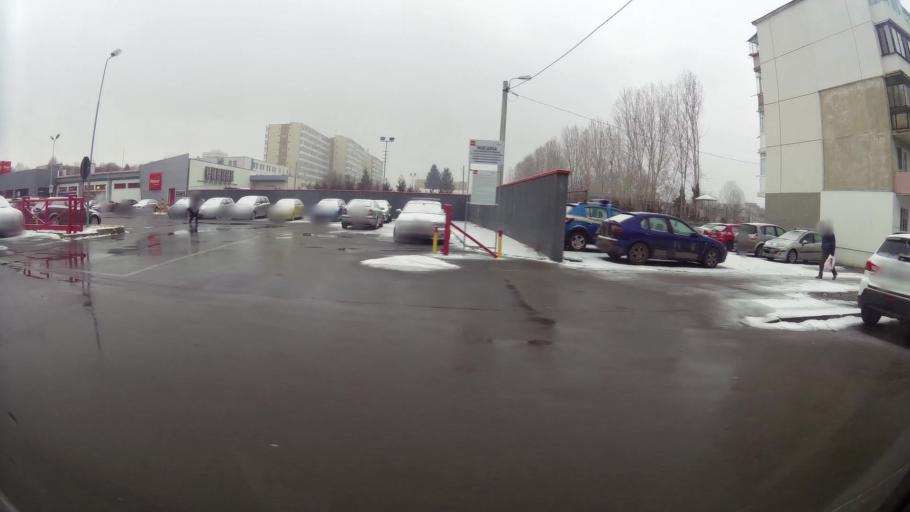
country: RO
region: Prahova
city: Ploiesti
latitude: 44.9346
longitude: 25.9909
